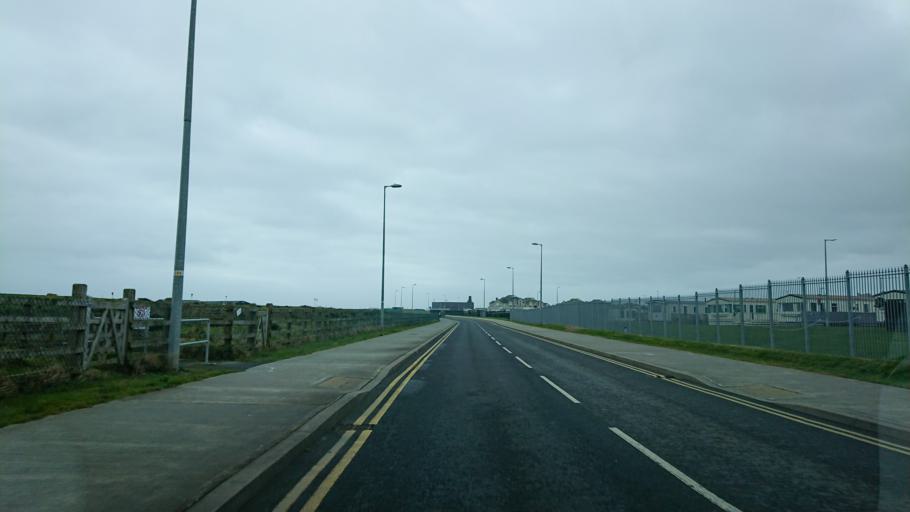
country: IE
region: Munster
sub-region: Waterford
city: Tra Mhor
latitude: 52.1632
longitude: -7.1345
